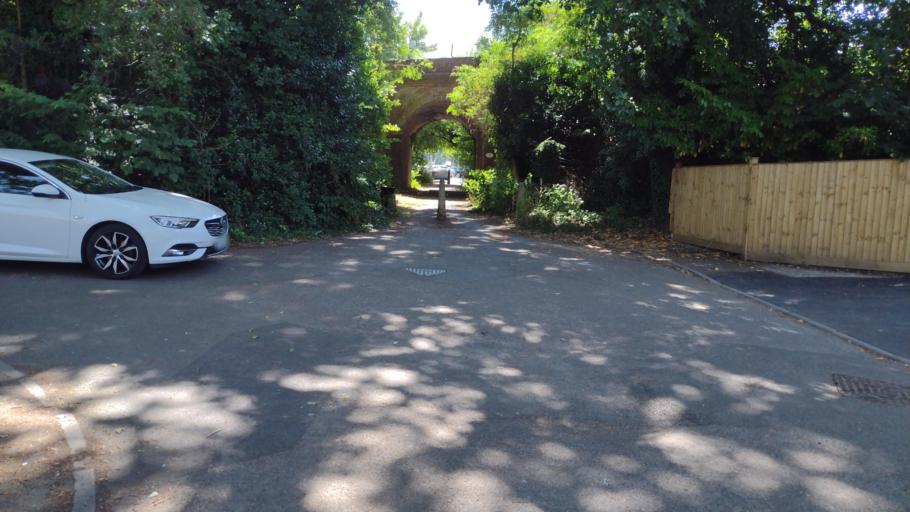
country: GB
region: England
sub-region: Bracknell Forest
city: Bracknell
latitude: 51.4099
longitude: -0.7337
